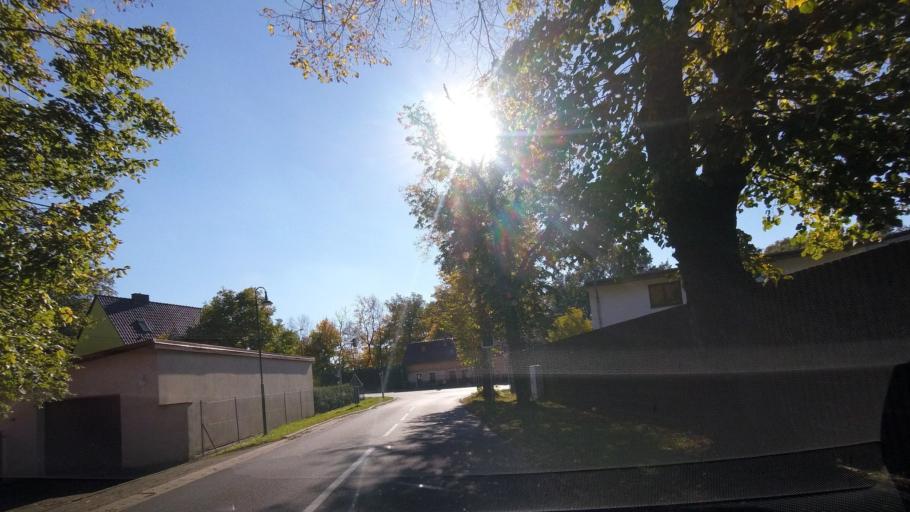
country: DE
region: Saxony-Anhalt
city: Muhlanger
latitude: 51.8547
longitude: 12.7475
